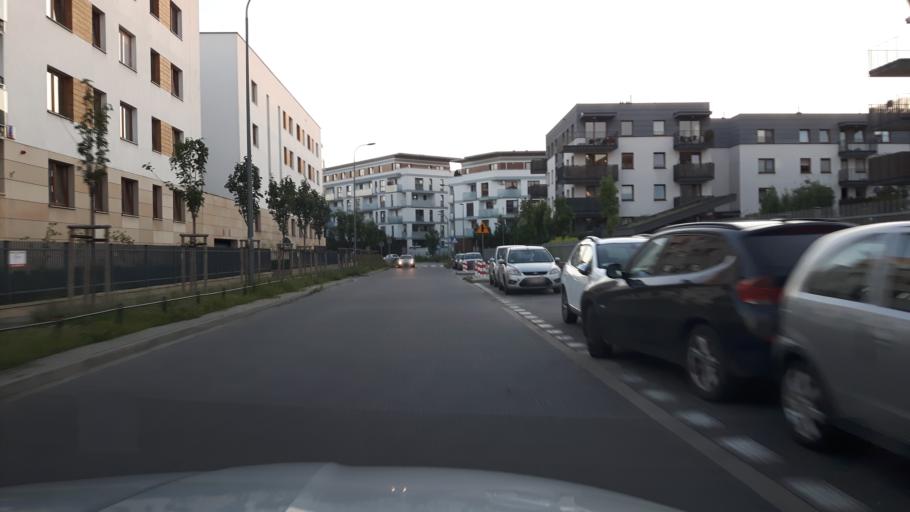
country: PL
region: Masovian Voivodeship
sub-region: Warszawa
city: Mokotow
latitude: 52.2086
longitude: 21.0648
